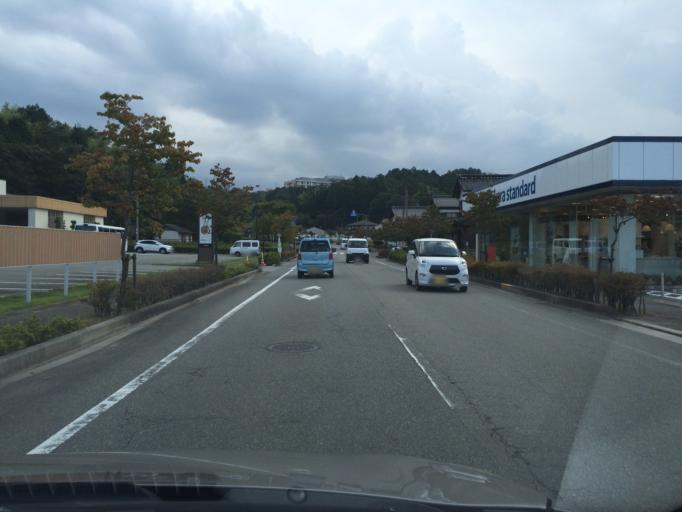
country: JP
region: Hyogo
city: Toyooka
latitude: 35.5329
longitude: 134.8080
